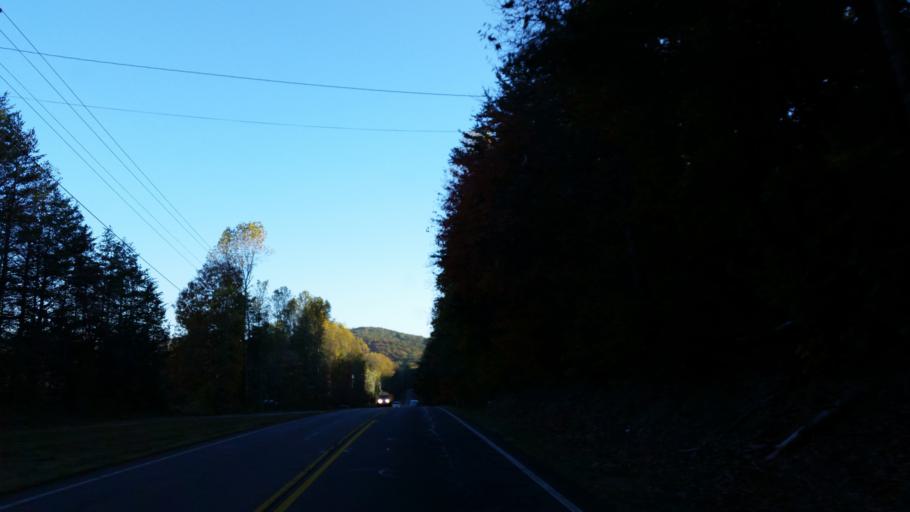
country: US
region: Georgia
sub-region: Pickens County
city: Jasper
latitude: 34.5877
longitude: -84.3069
